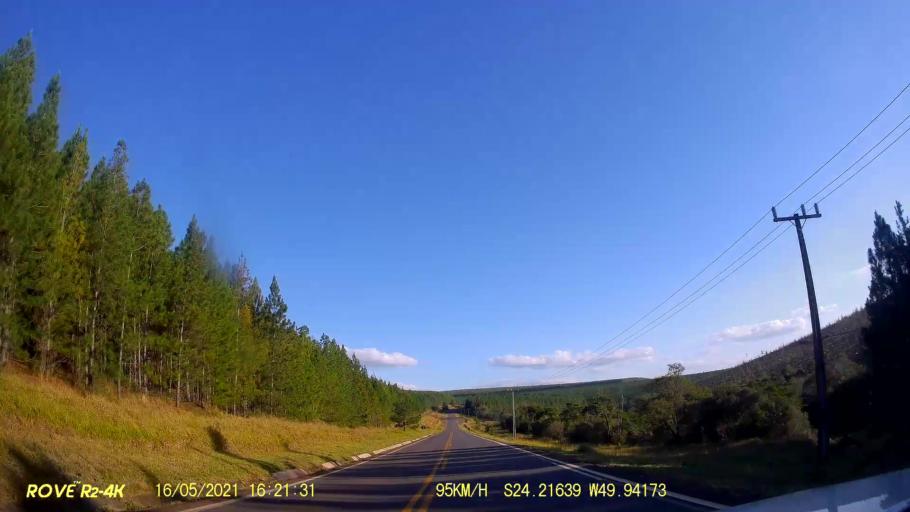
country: BR
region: Parana
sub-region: Jaguariaiva
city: Jaguariaiva
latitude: -24.2166
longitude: -49.9419
